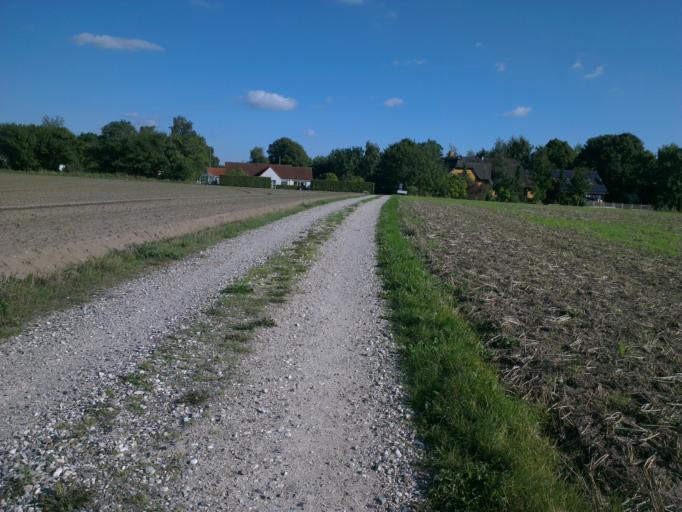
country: DK
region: Capital Region
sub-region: Frederikssund Kommune
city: Jaegerspris
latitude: 55.8371
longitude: 11.9825
